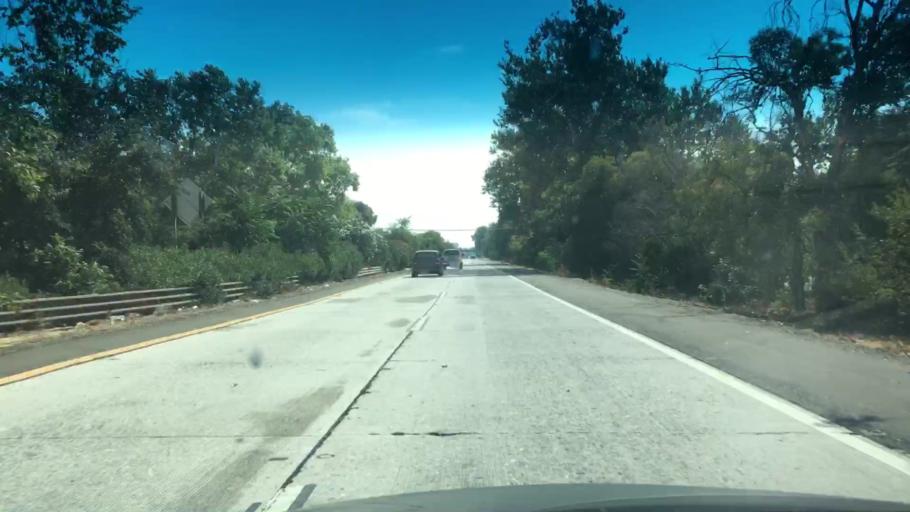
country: US
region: California
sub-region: Sacramento County
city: Sacramento
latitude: 38.6001
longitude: -121.4659
